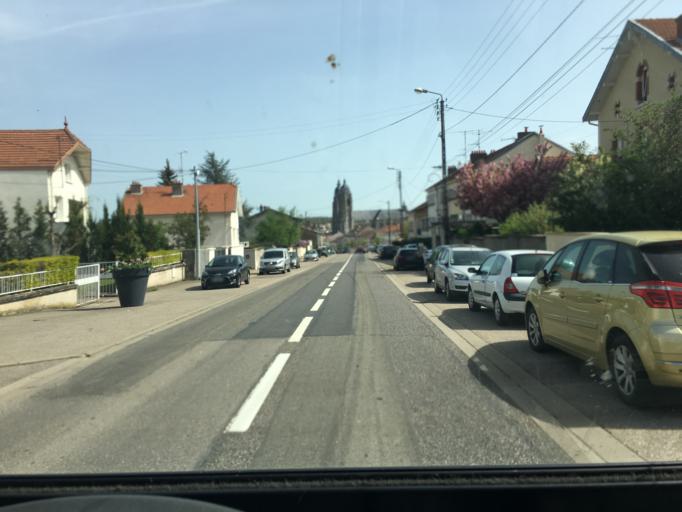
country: FR
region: Lorraine
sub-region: Departement de Meurthe-et-Moselle
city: Saint-Nicolas-de-Port
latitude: 48.6286
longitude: 6.2972
